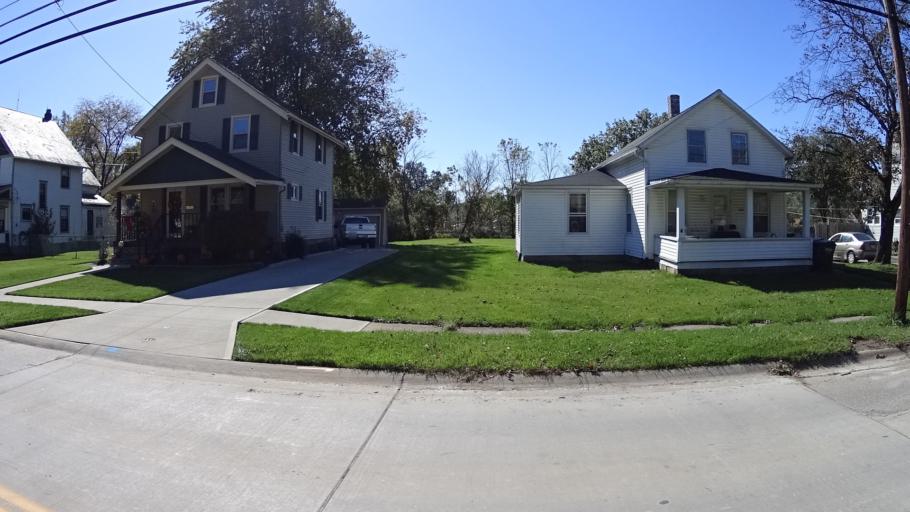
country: US
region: Ohio
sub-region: Lorain County
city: Amherst
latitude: 41.3911
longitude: -82.2206
